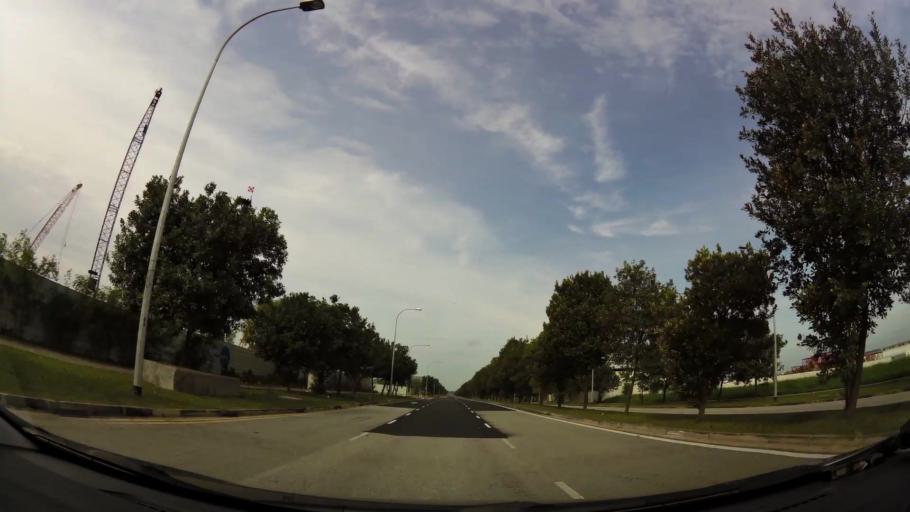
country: SG
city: Singapore
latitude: 1.2744
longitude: 103.6287
